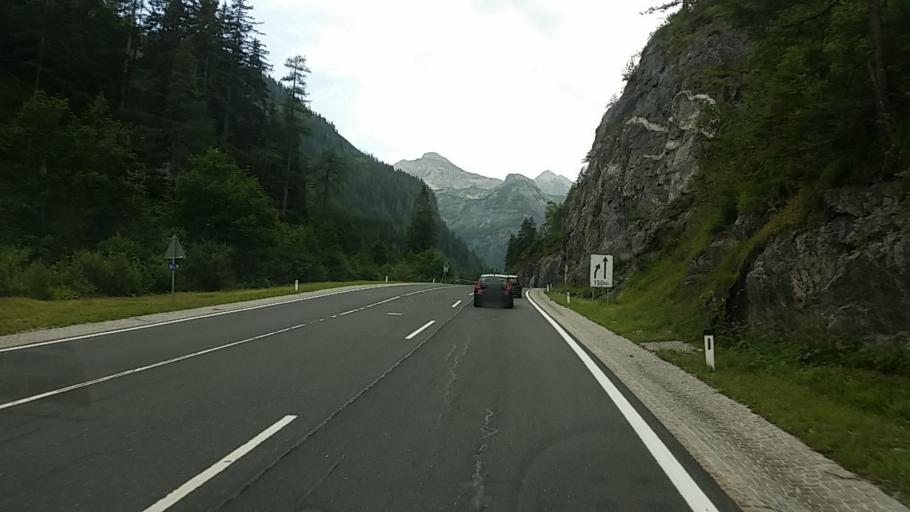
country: AT
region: Salzburg
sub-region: Politischer Bezirk Sankt Johann im Pongau
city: Untertauern
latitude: 47.2716
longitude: 13.5003
